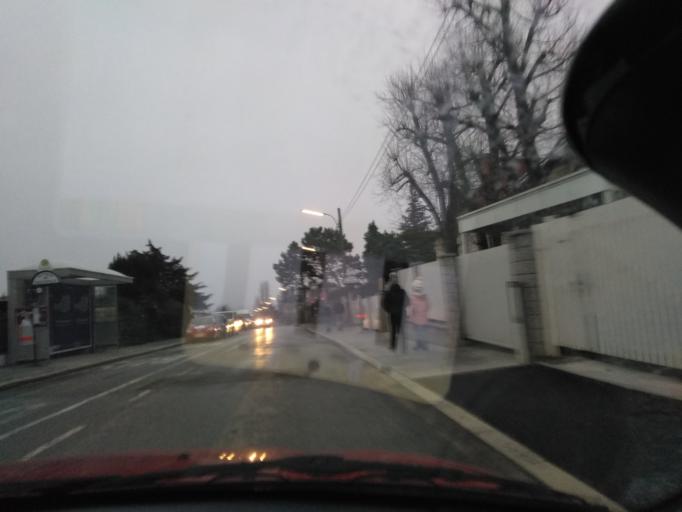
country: AT
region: Vienna
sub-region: Wien Stadt
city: Vienna
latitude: 48.2334
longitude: 16.3049
